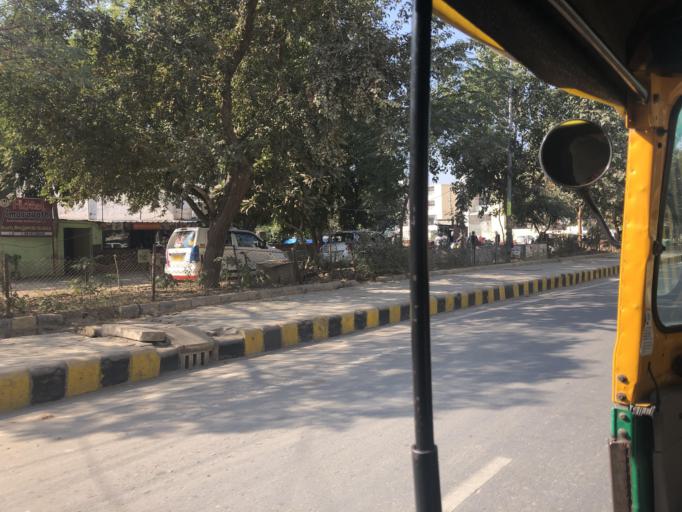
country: IN
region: Haryana
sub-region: Gurgaon
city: Gurgaon
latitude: 28.4496
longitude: 77.0705
